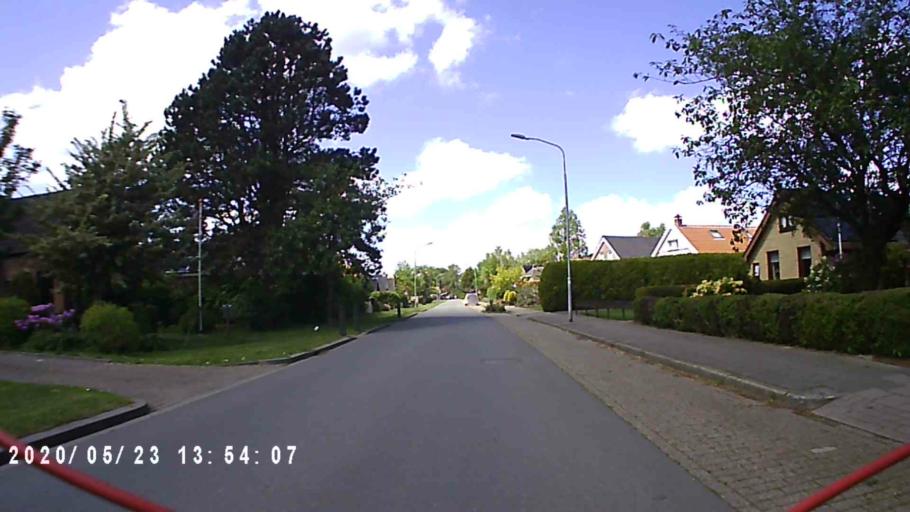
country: NL
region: Groningen
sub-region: Gemeente  Oldambt
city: Winschoten
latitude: 53.2712
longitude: 7.0328
